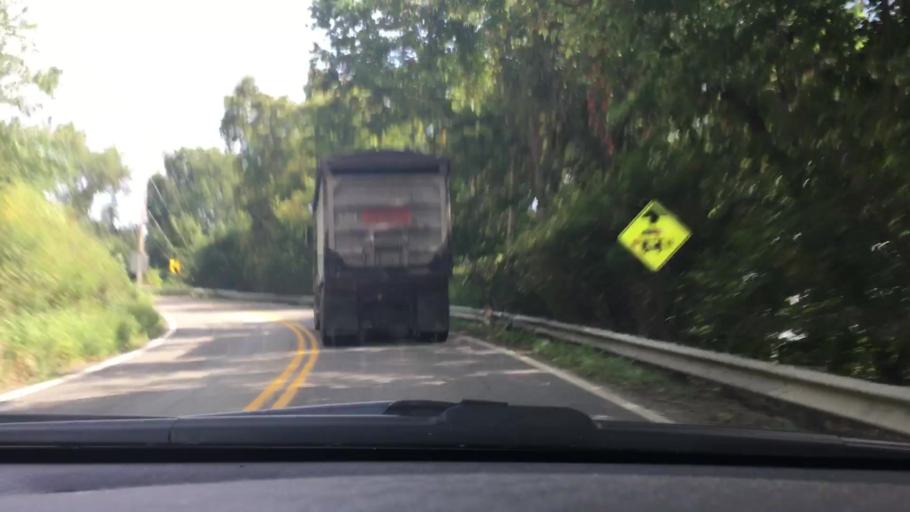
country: US
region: Pennsylvania
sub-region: Washington County
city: New Eagle
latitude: 40.2497
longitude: -79.9522
